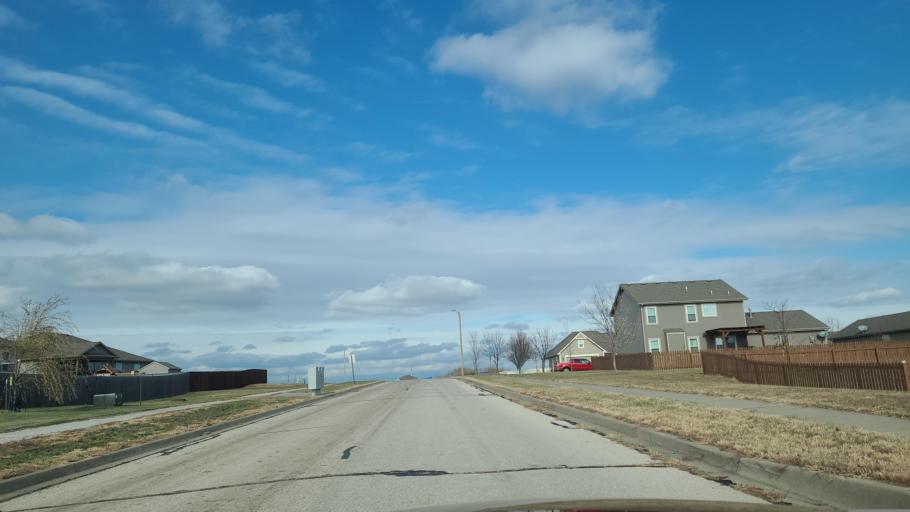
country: US
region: Kansas
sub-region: Douglas County
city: Eudora
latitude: 38.9174
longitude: -95.1013
